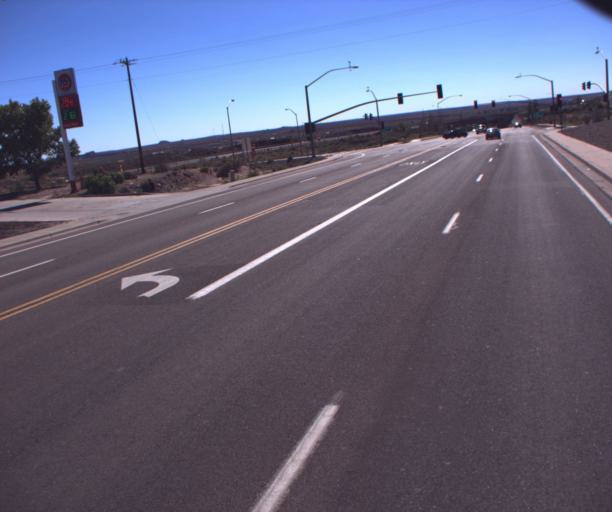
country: US
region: Arizona
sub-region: Navajo County
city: Holbrook
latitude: 34.9156
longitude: -110.1542
